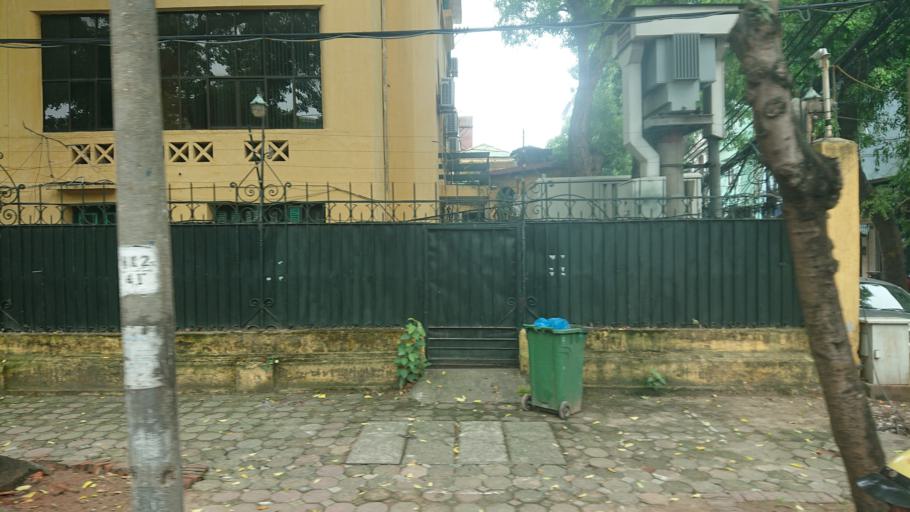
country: VN
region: Ha Noi
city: Hanoi
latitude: 21.0211
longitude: 105.8449
